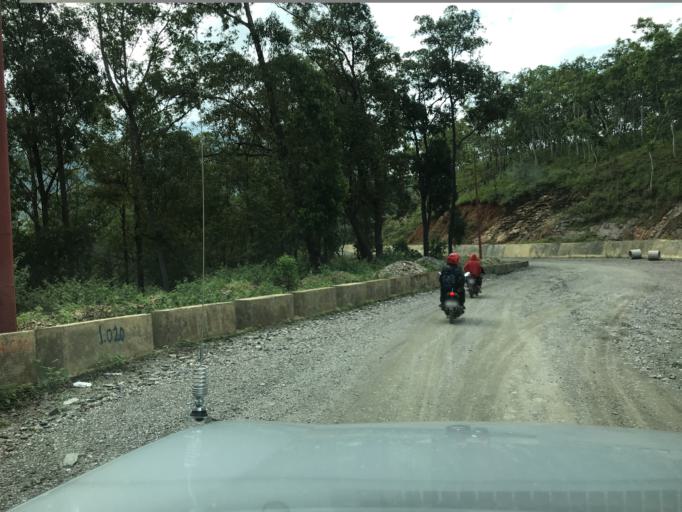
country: TL
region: Aileu
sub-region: Aileu Villa
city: Aileu
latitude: -8.6635
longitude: 125.5342
